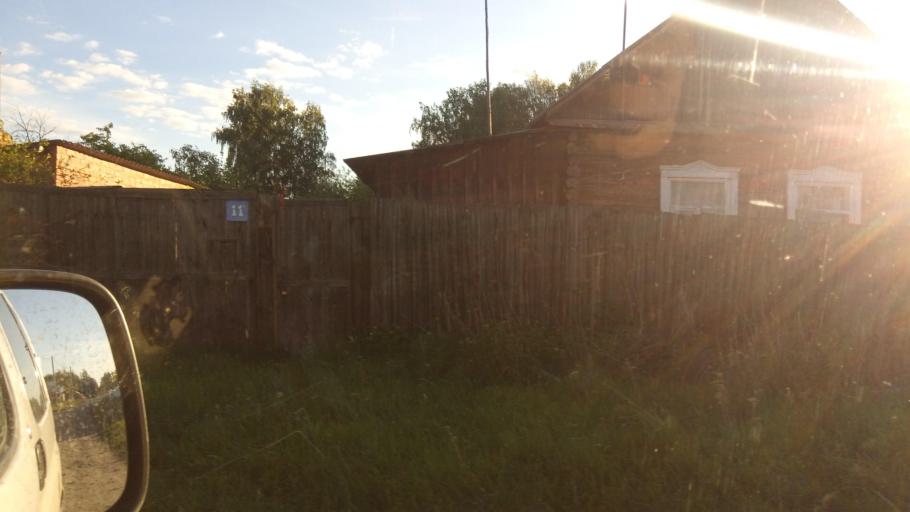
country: RU
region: Chelyabinsk
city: Timiryazevskiy
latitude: 54.9877
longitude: 60.8424
